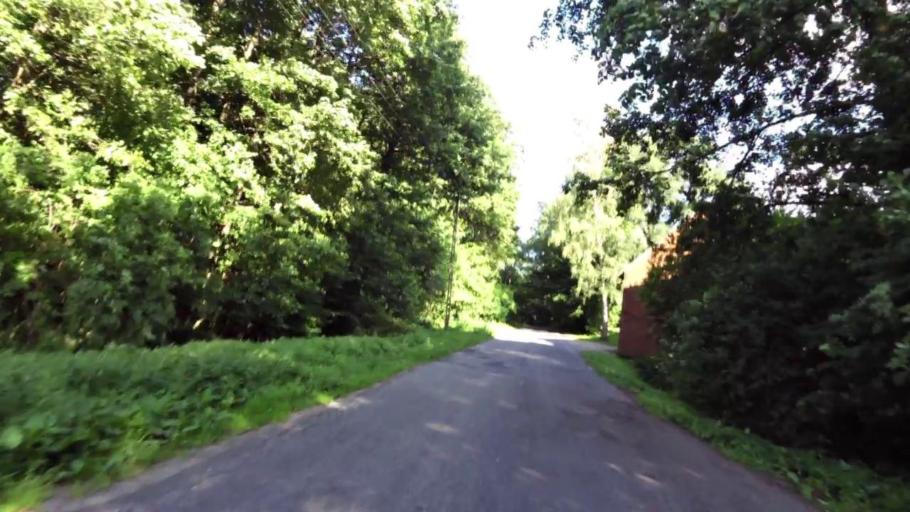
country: PL
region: West Pomeranian Voivodeship
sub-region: Powiat slawienski
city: Slawno
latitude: 54.4351
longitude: 16.7671
